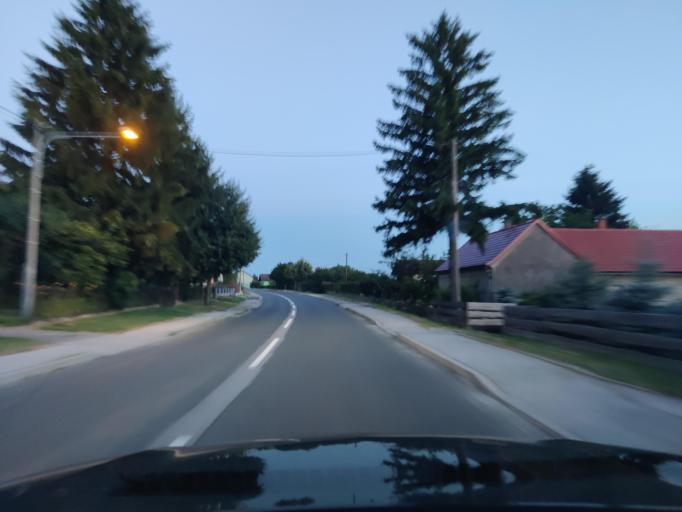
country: SI
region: Lendava-Lendva
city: Lendava
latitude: 46.5785
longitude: 16.4460
